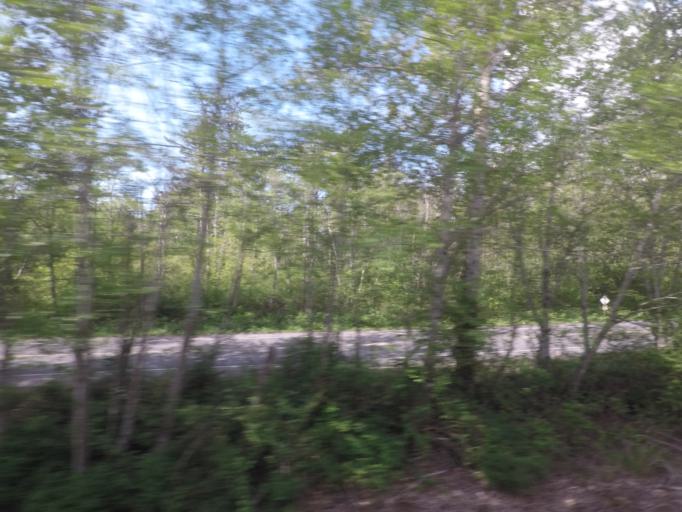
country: US
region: Washington
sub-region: Whatcom County
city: Marietta-Alderwood
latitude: 48.7876
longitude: -122.5579
